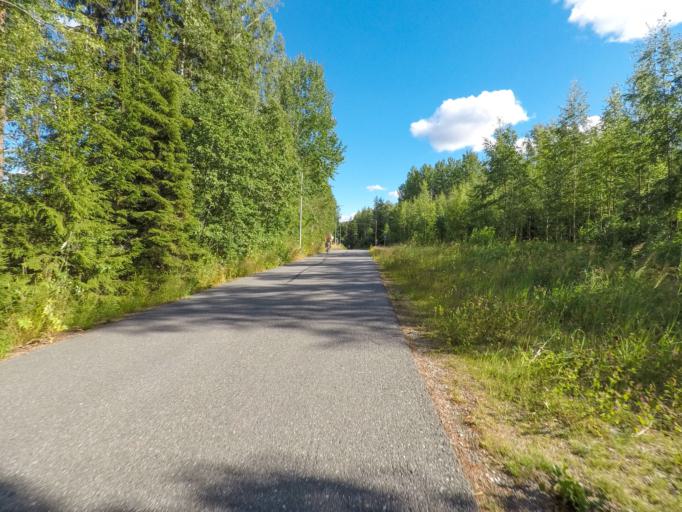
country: FI
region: South Karelia
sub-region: Lappeenranta
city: Lappeenranta
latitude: 61.0955
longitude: 28.1374
